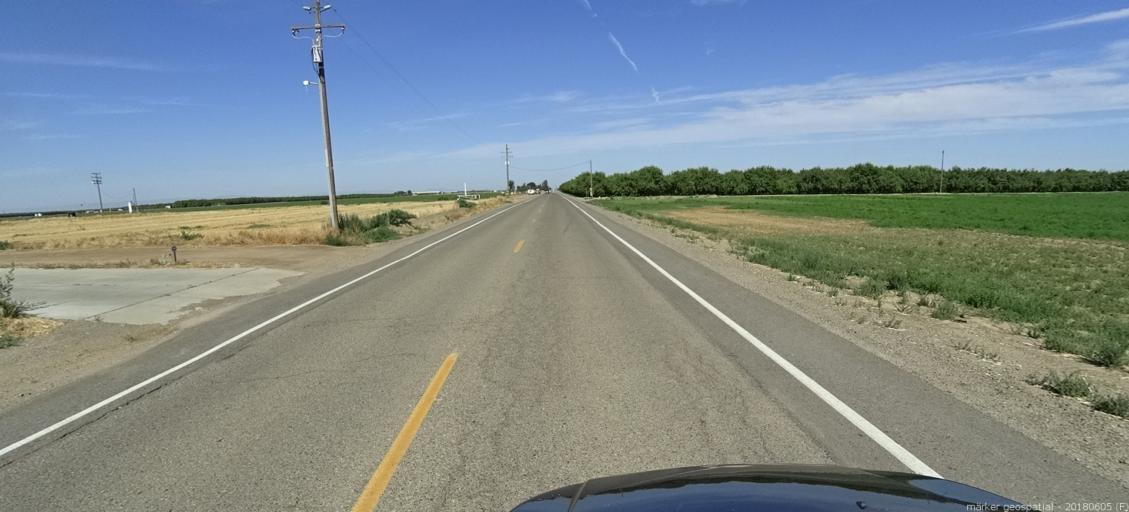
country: US
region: California
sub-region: Madera County
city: Chowchilla
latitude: 37.1127
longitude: -120.3683
